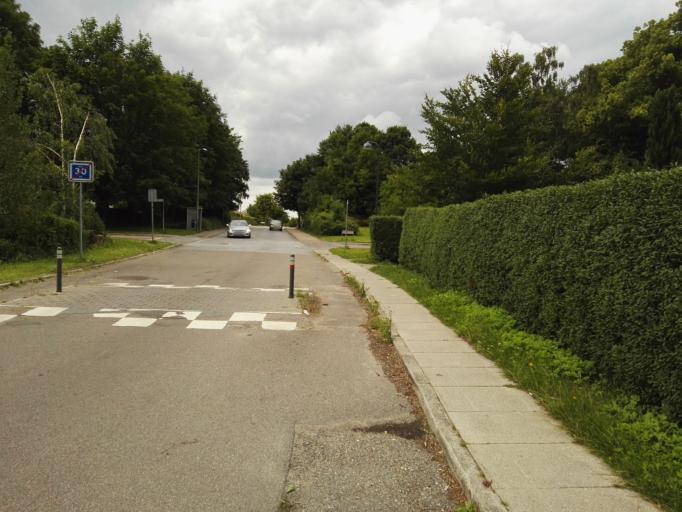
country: DK
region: Capital Region
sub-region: Egedal Kommune
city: Olstykke
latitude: 55.7816
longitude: 12.1717
